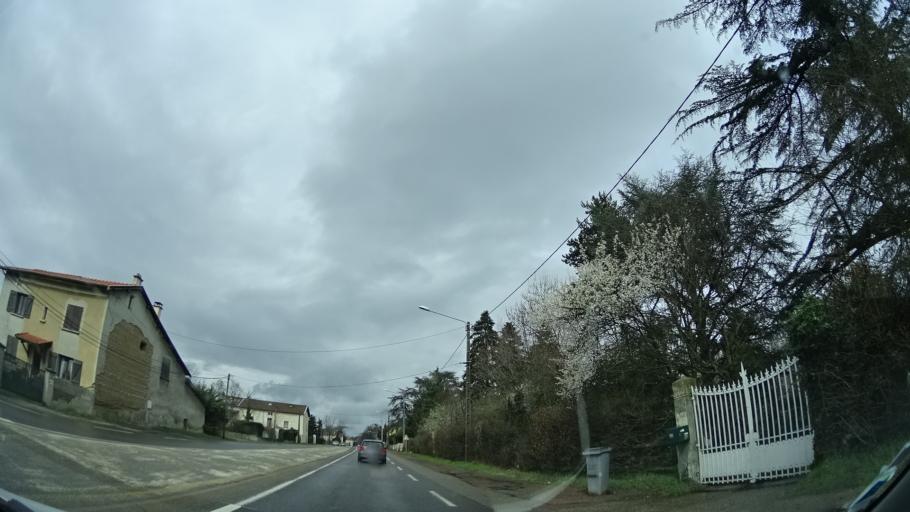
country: FR
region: Rhone-Alpes
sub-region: Departement du Rhone
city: Charbonnieres-les-Bains
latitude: 45.7953
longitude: 4.7414
